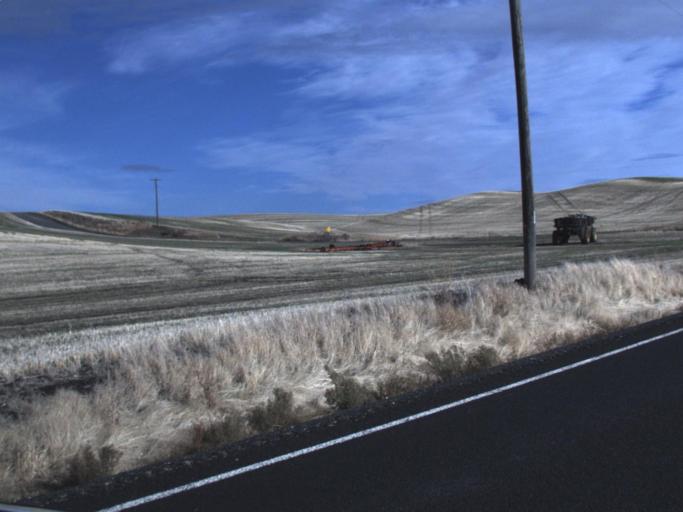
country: US
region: Washington
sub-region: Whitman County
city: Colfax
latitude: 46.9380
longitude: -117.1871
